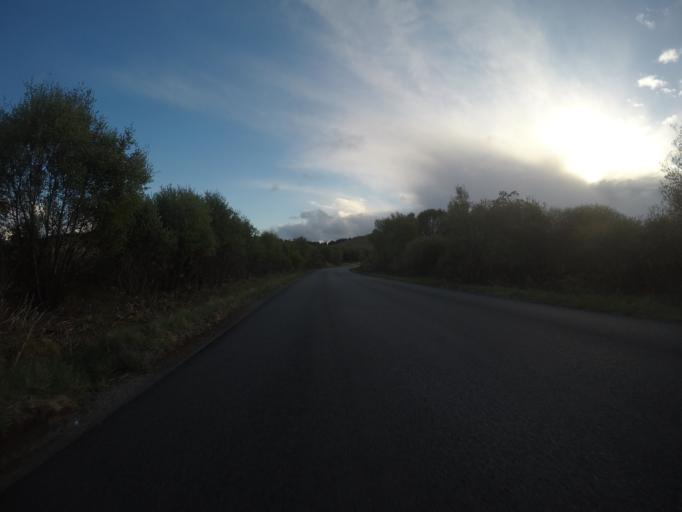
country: GB
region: Scotland
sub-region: Highland
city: Isle of Skye
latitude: 57.4528
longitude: -6.2998
